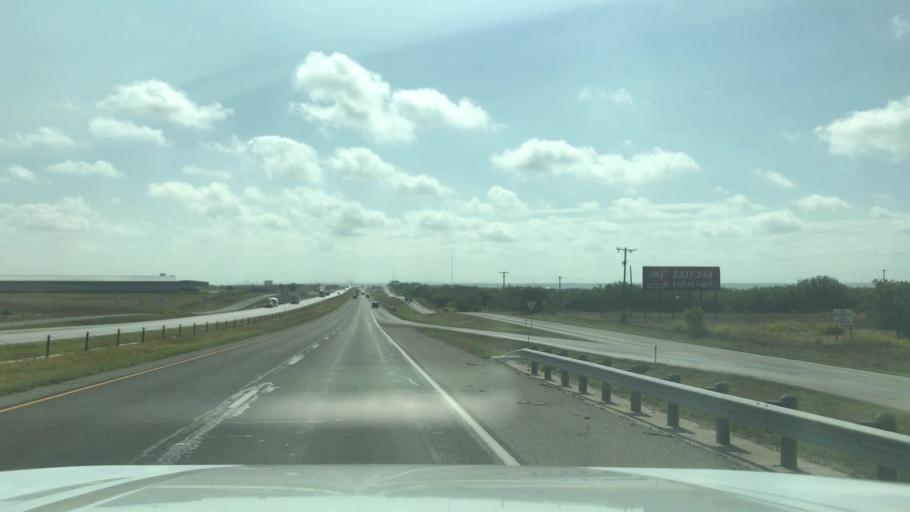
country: US
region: Texas
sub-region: Nolan County
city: Sweetwater
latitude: 32.4496
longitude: -100.4397
